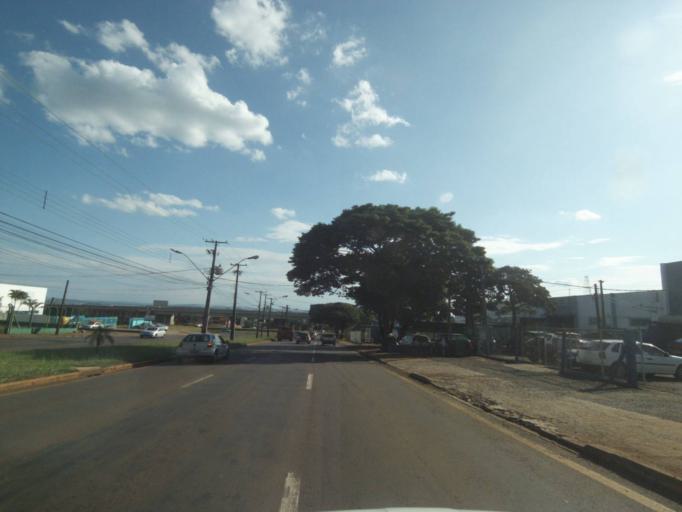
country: BR
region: Parana
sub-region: Londrina
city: Londrina
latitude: -23.3589
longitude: -51.1511
